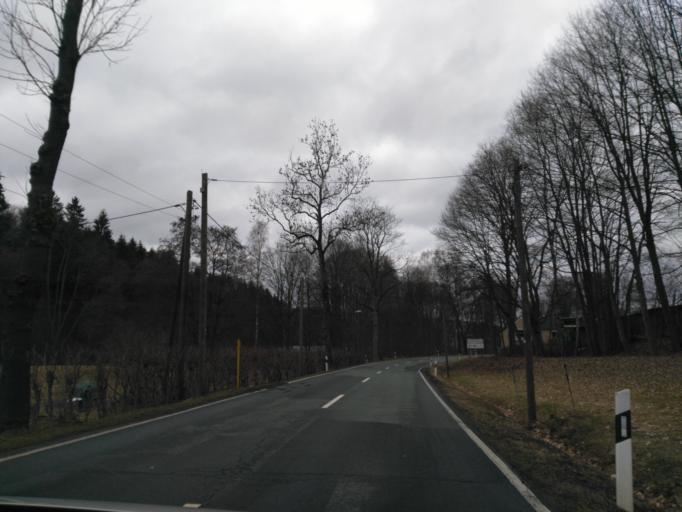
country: DE
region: Saxony
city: Ehrenfriedersdorf
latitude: 50.6655
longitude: 12.9673
